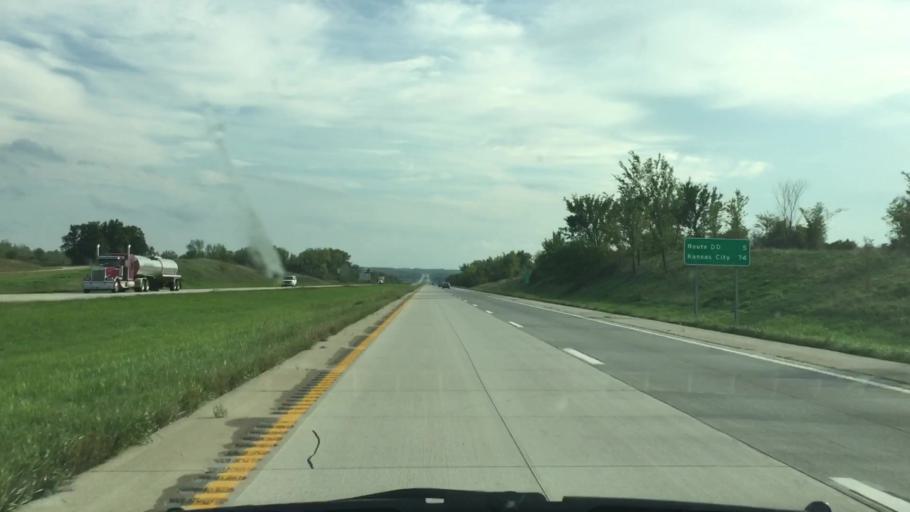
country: US
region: Missouri
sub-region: Daviess County
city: Gallatin
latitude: 40.0652
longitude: -94.0940
